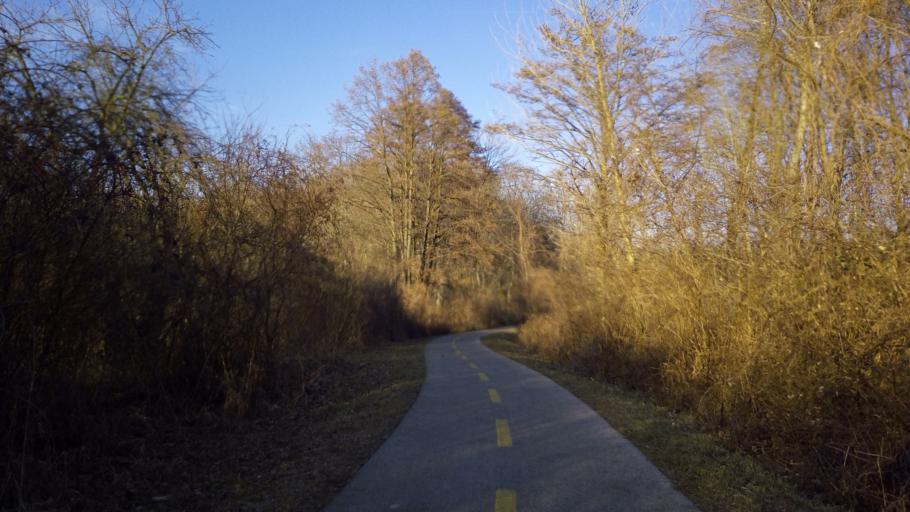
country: HU
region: Baranya
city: Pellerd
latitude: 46.0365
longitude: 18.1707
